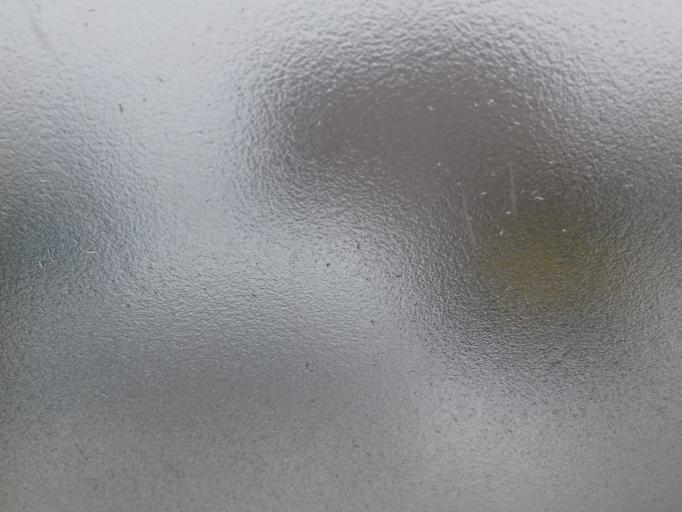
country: BA
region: Federation of Bosnia and Herzegovina
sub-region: Kanton Sarajevo
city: Sarajevo
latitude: 43.8325
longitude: 18.2891
